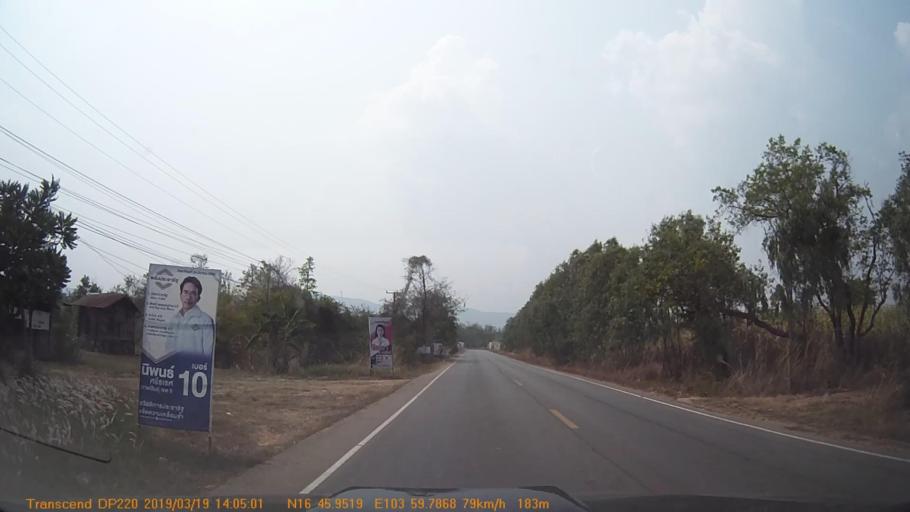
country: TH
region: Kalasin
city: Na Khu
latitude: 16.7660
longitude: 103.9960
